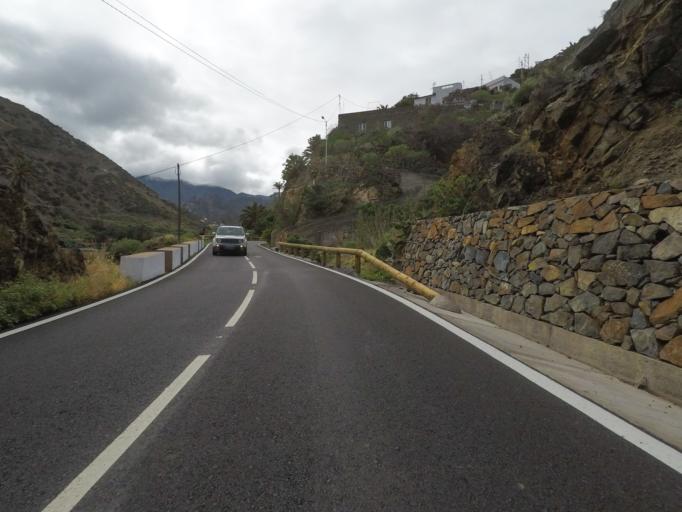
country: ES
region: Canary Islands
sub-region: Provincia de Santa Cruz de Tenerife
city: Vallehermosa
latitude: 28.1908
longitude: -17.2620
